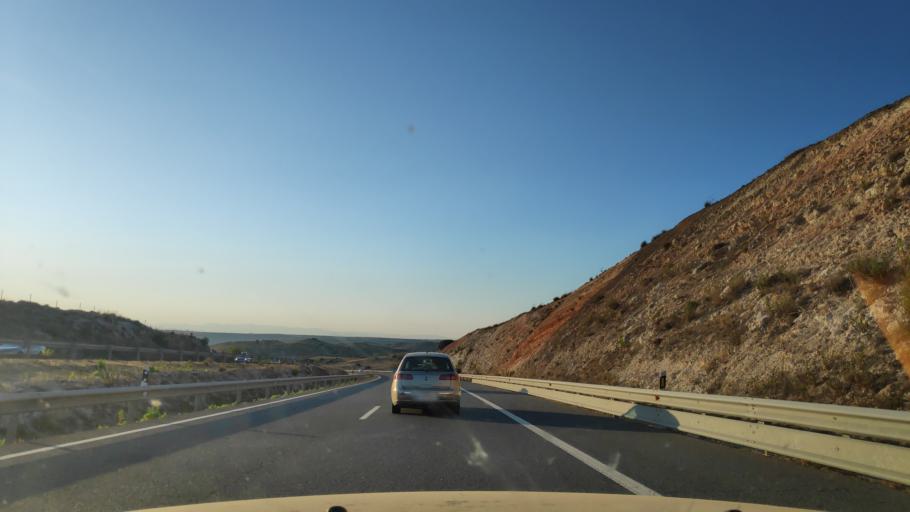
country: ES
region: Madrid
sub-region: Provincia de Madrid
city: Villarejo de Salvanes
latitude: 40.1905
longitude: -3.2993
